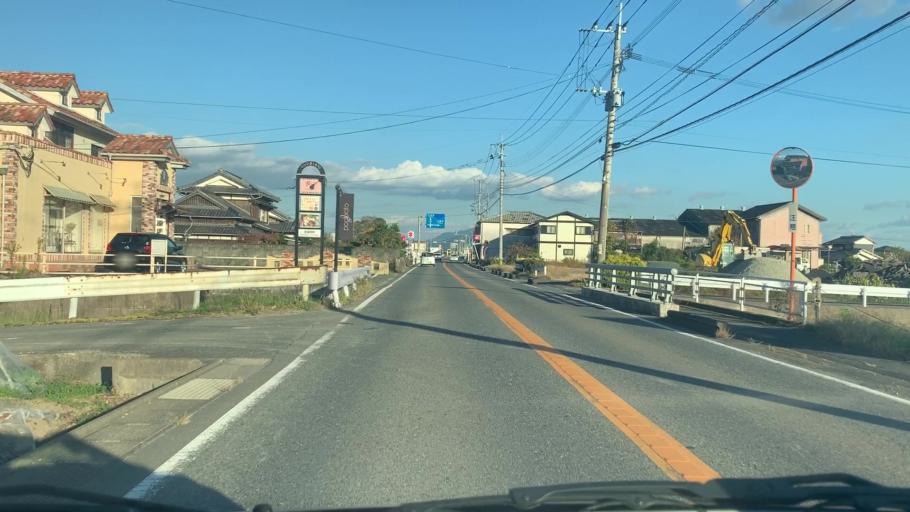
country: JP
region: Saga Prefecture
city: Kanzakimachi-kanzaki
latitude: 33.2974
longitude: 130.4413
